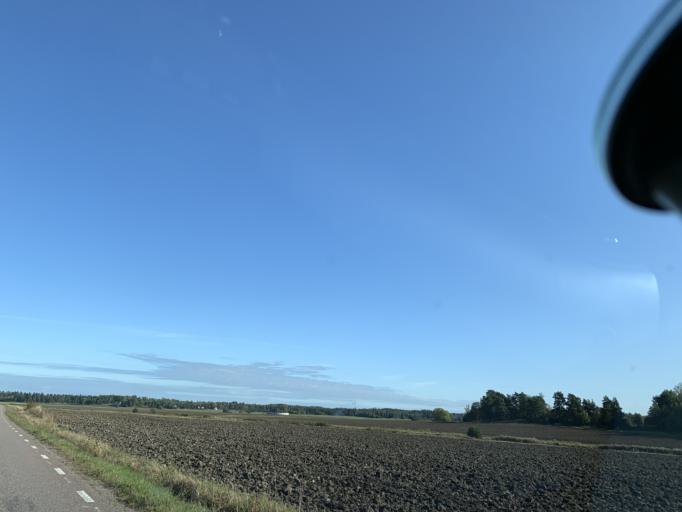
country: SE
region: Soedermanland
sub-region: Eskilstuna Kommun
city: Kvicksund
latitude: 59.5526
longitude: 16.4107
